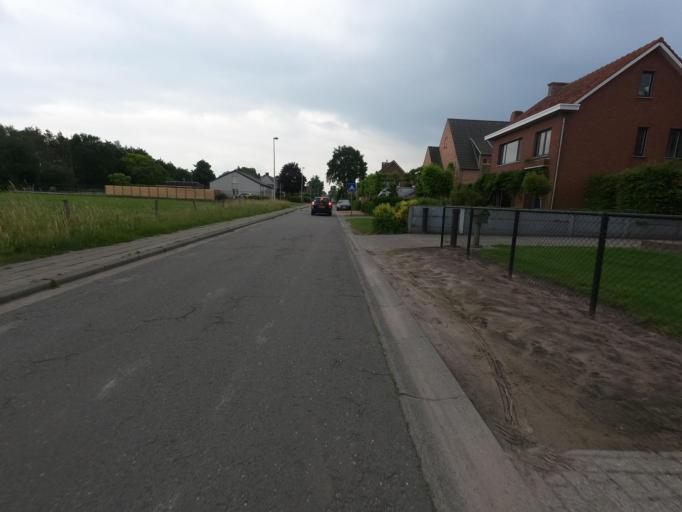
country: BE
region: Flanders
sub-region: Provincie Antwerpen
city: Essen
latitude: 51.4694
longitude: 4.4929
